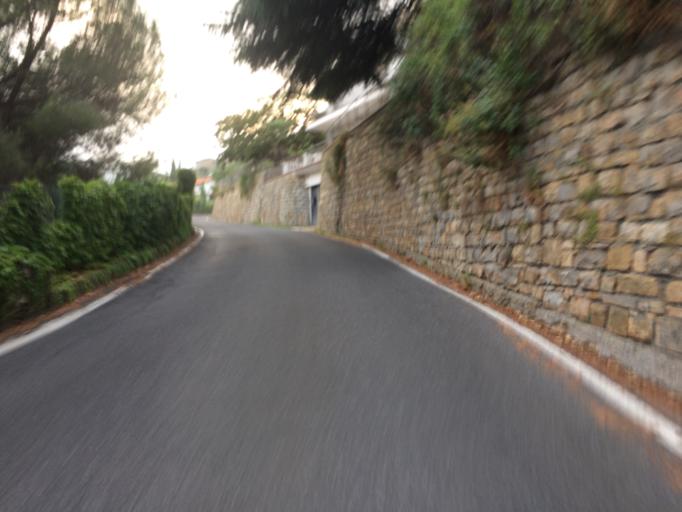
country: IT
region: Liguria
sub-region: Provincia di Imperia
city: San Remo
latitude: 43.8432
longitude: 7.7450
